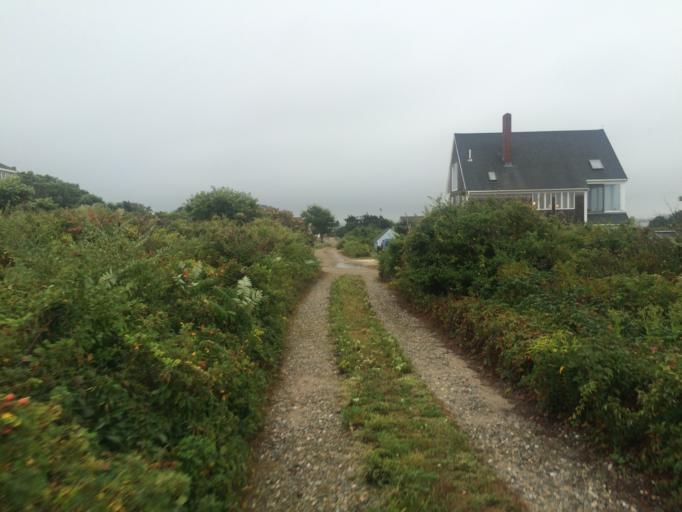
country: US
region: Massachusetts
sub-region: Plymouth County
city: Duxbury
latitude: 42.0050
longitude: -70.6004
